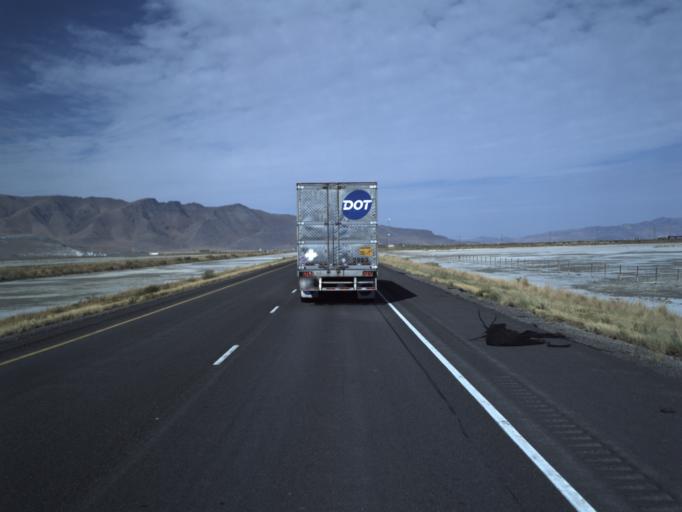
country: US
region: Utah
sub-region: Tooele County
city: Grantsville
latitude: 40.7034
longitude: -112.5013
